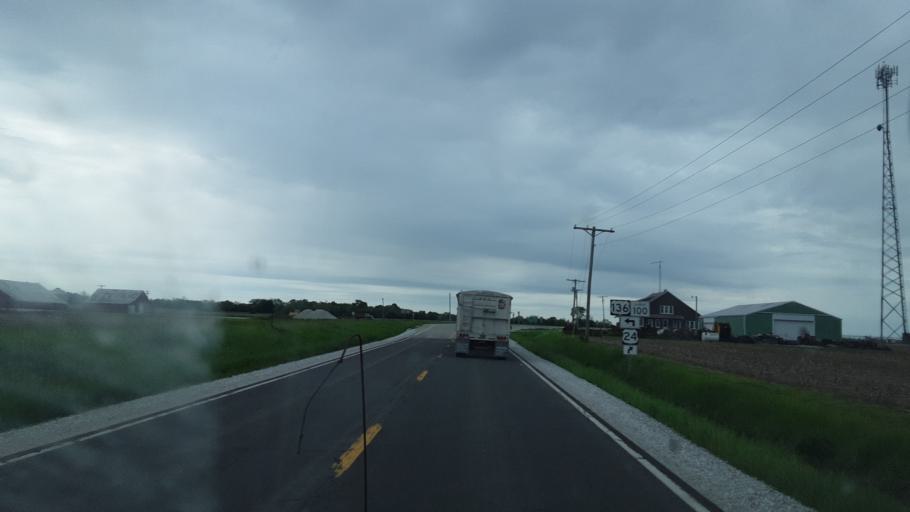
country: US
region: Illinois
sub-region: Fulton County
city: Lewistown
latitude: 40.3069
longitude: -90.1909
